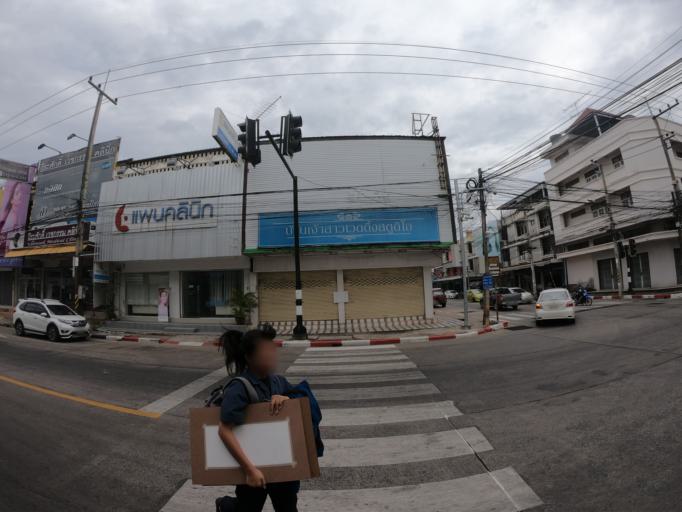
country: TH
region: Roi Et
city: Roi Et
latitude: 16.0571
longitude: 103.6569
